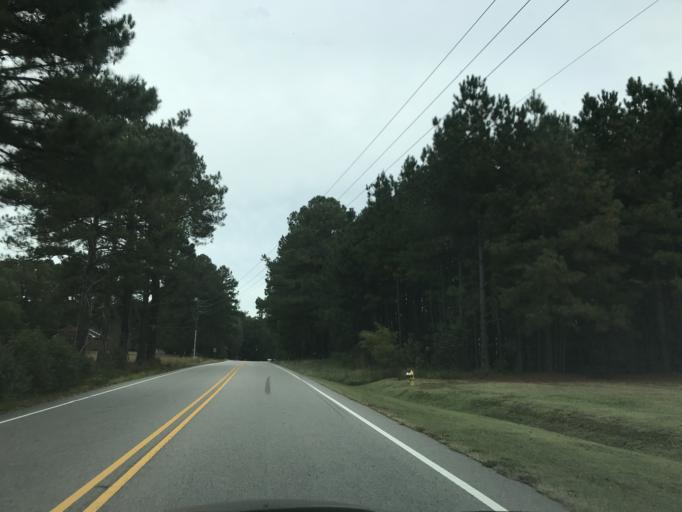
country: US
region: North Carolina
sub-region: Wake County
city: Knightdale
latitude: 35.8507
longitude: -78.5117
